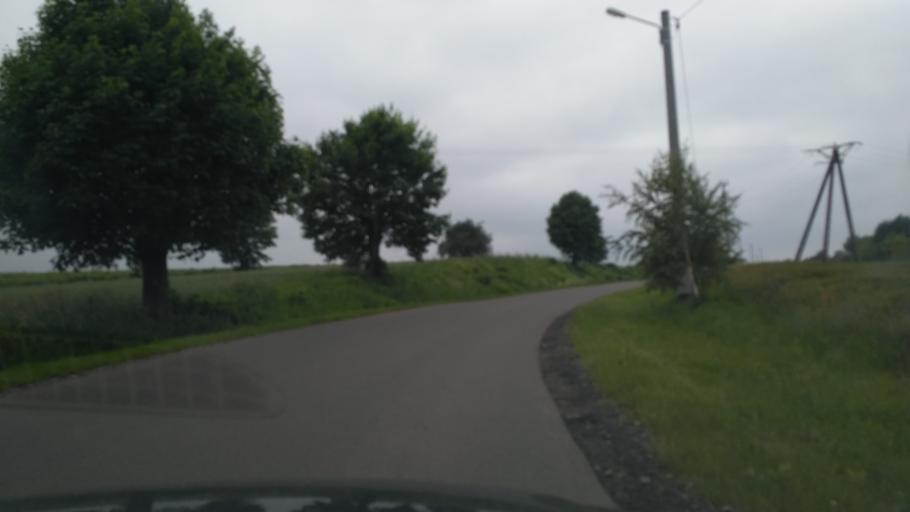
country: PL
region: Subcarpathian Voivodeship
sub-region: Powiat ropczycko-sedziszowski
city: Sedziszow Malopolski
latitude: 50.0484
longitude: 21.6931
